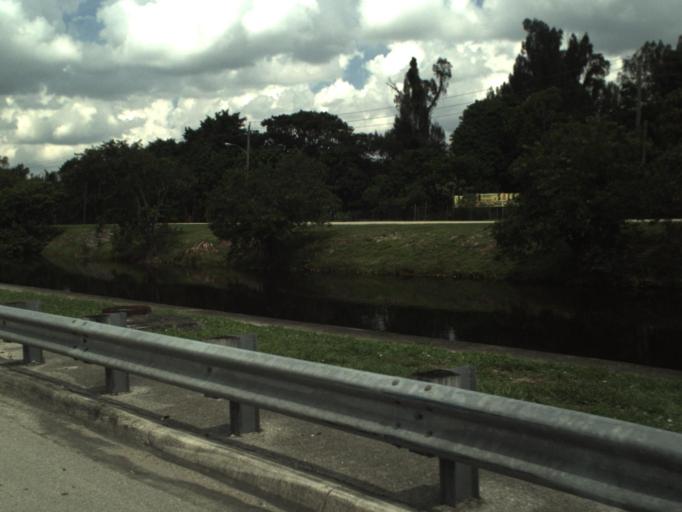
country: US
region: Florida
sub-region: Broward County
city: Cooper City
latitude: 26.0644
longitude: -80.2716
